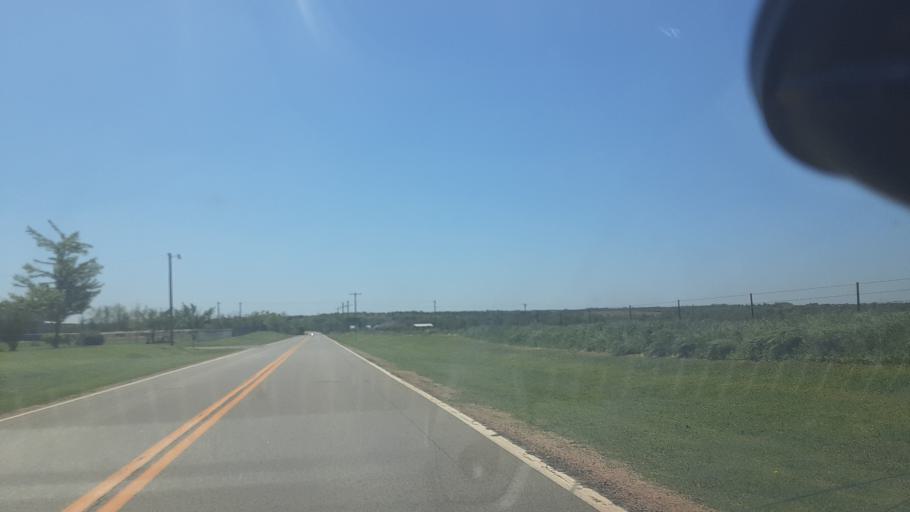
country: US
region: Oklahoma
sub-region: Logan County
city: Guthrie
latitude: 36.0593
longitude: -97.4072
